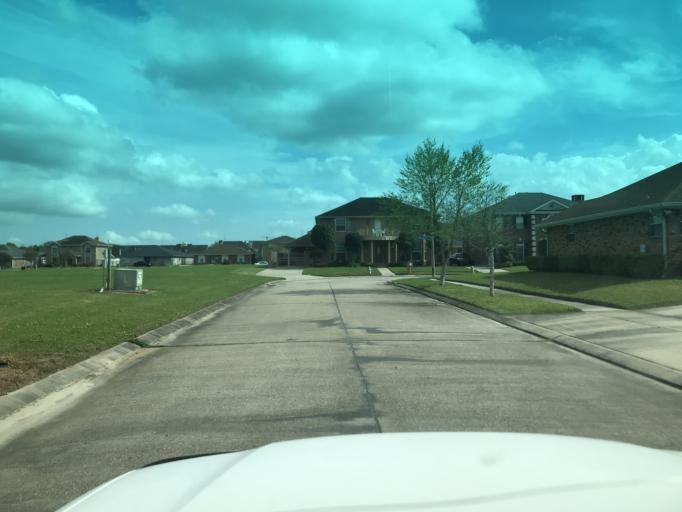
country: US
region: Louisiana
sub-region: Saint Bernard Parish
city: Chalmette
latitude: 30.0326
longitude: -89.9522
